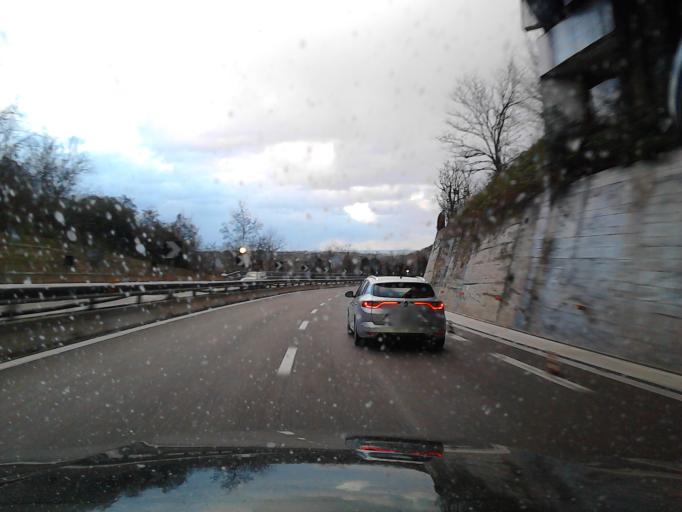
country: IT
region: Abruzzo
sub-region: Provincia di Chieti
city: Treglio
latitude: 42.2703
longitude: 14.4342
